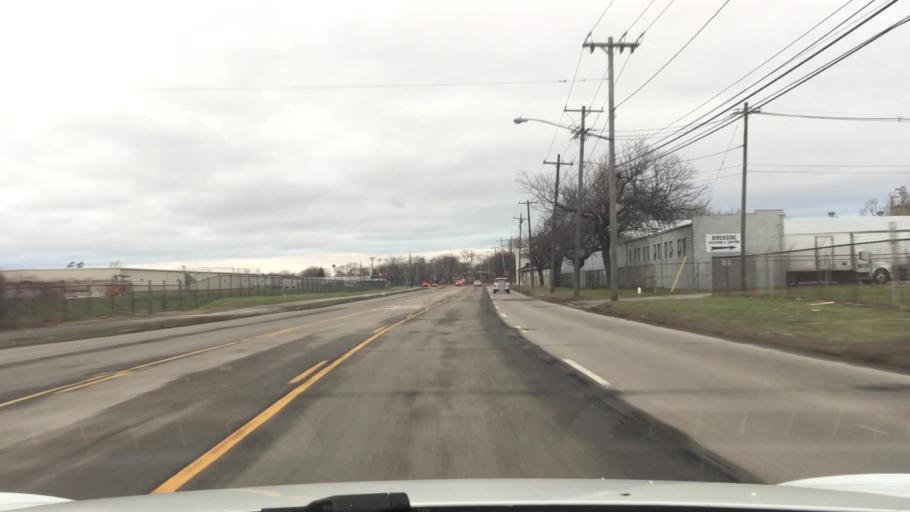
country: US
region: New York
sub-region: Erie County
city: Tonawanda
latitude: 43.0433
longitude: -78.8886
